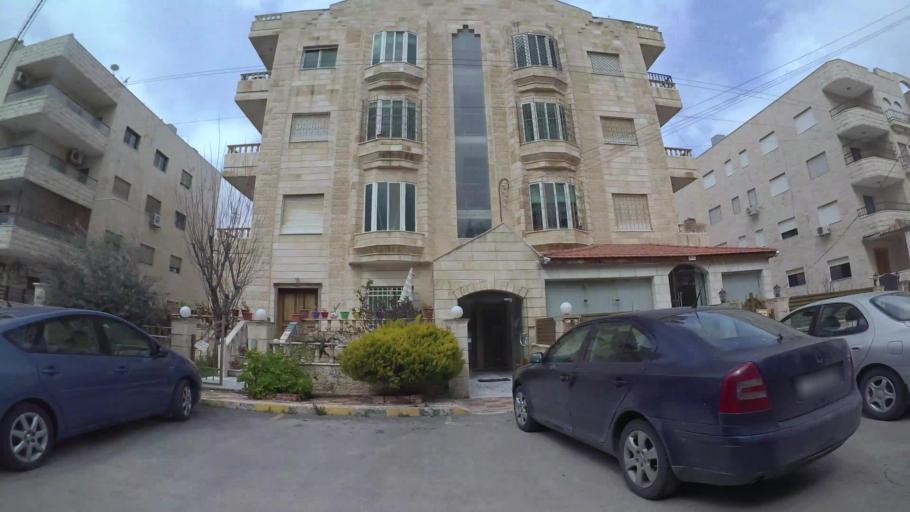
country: JO
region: Amman
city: Umm as Summaq
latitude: 31.8969
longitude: 35.8618
